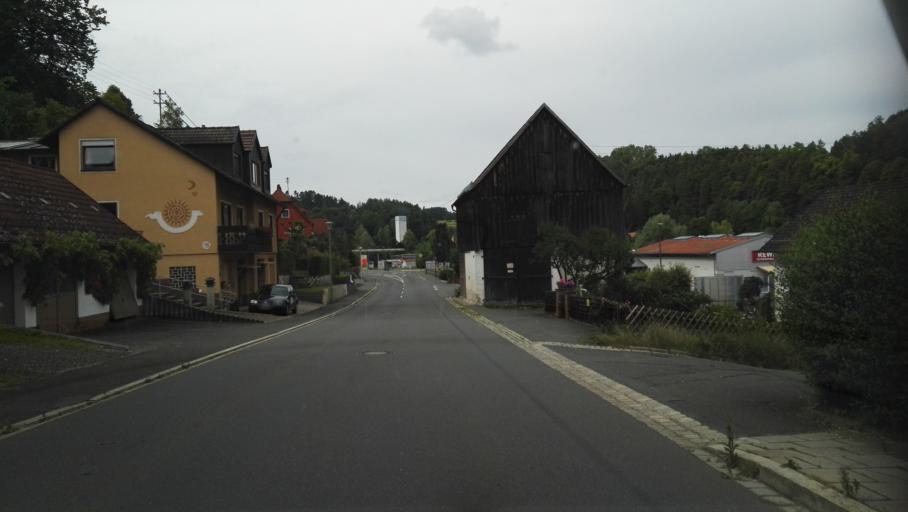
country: DE
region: Bavaria
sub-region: Upper Franconia
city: Waischenfeld
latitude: 49.8473
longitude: 11.3435
